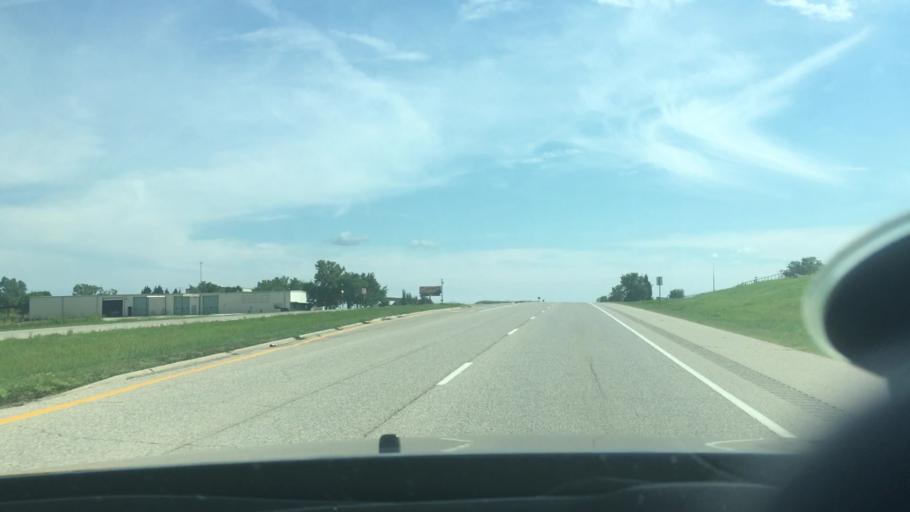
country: US
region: Oklahoma
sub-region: Seminole County
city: Seminole
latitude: 35.1992
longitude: -96.6751
